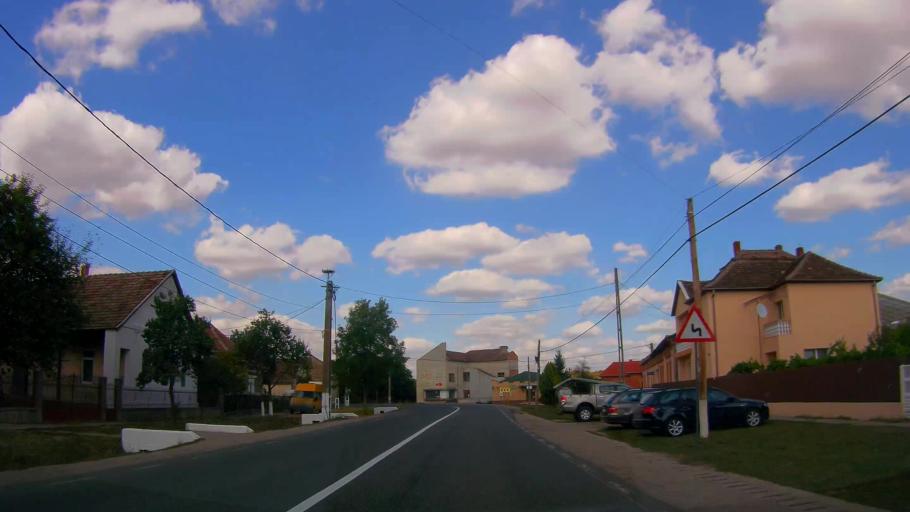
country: RO
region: Satu Mare
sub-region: Comuna Beltiug
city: Beltiug
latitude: 47.5482
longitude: 22.8404
